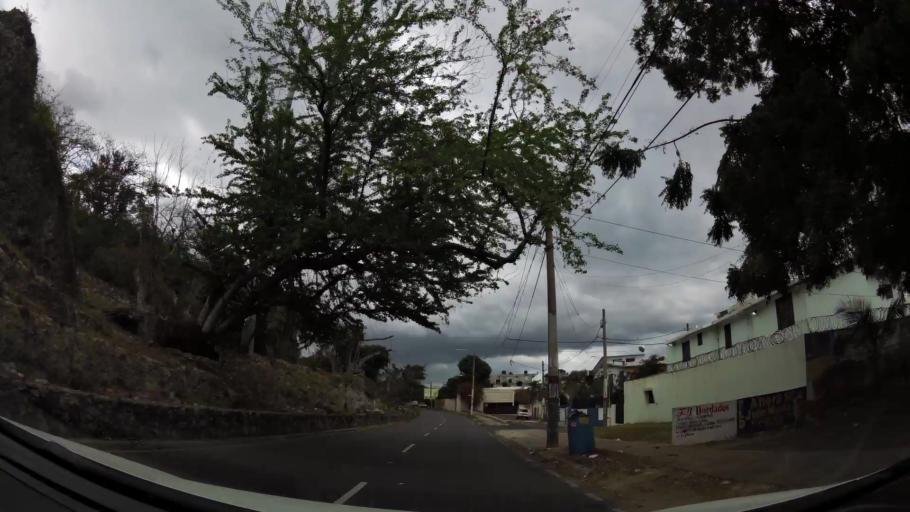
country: DO
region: Nacional
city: Bella Vista
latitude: 18.4419
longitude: -69.9533
